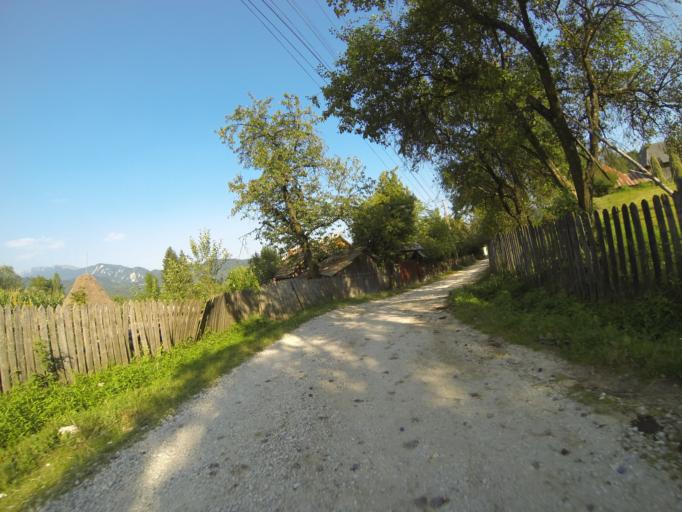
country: RO
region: Valcea
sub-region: Comuna Horezu
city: Horezu
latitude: 45.1867
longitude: 23.9888
